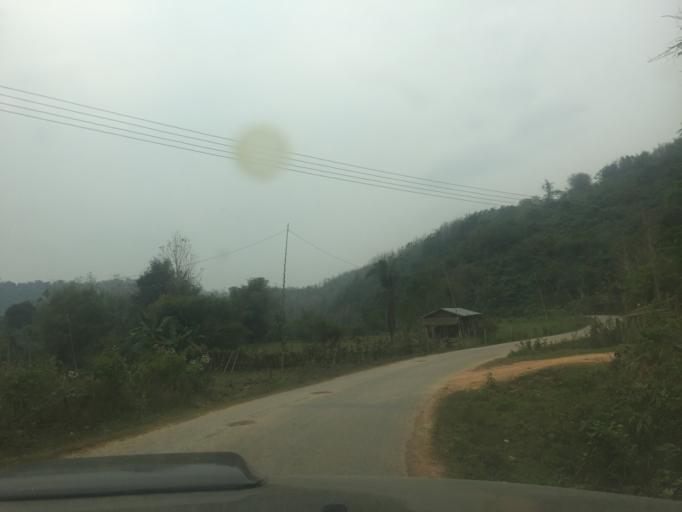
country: LA
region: Vientiane
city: Muang Sanakham
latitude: 18.3967
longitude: 101.5188
